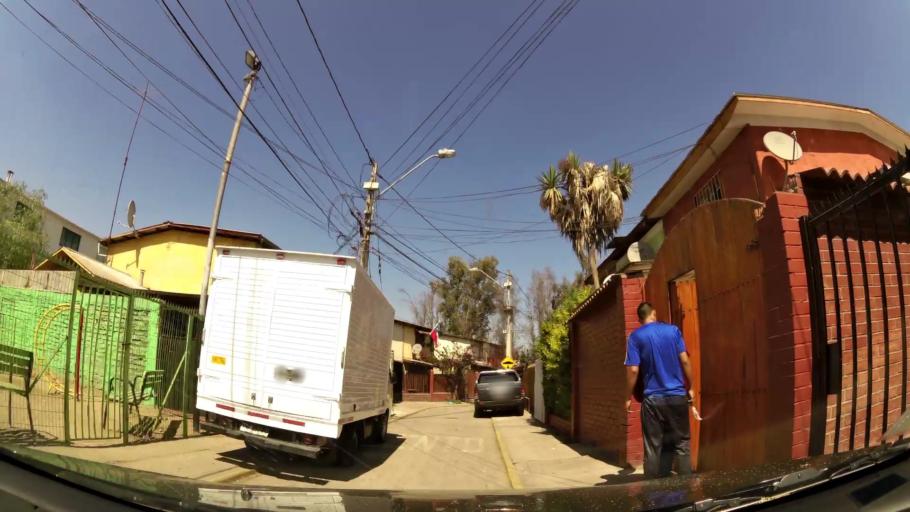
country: CL
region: Santiago Metropolitan
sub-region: Provincia de Santiago
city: Lo Prado
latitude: -33.3648
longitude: -70.7461
